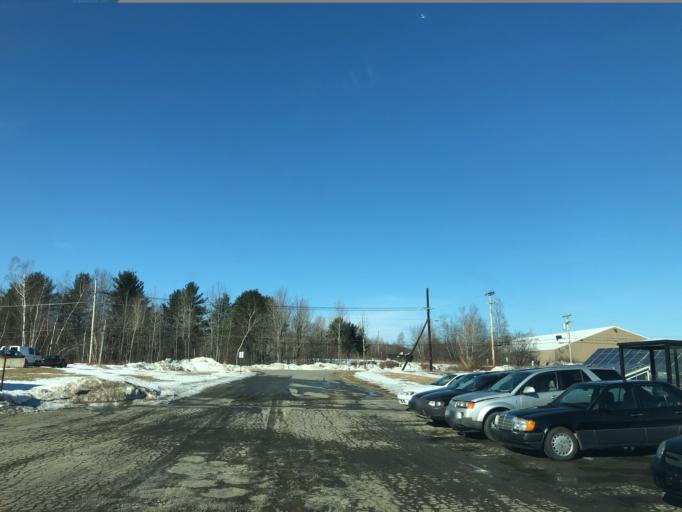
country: US
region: Maine
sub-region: Penobscot County
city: Brewer
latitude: 44.8242
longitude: -68.7436
